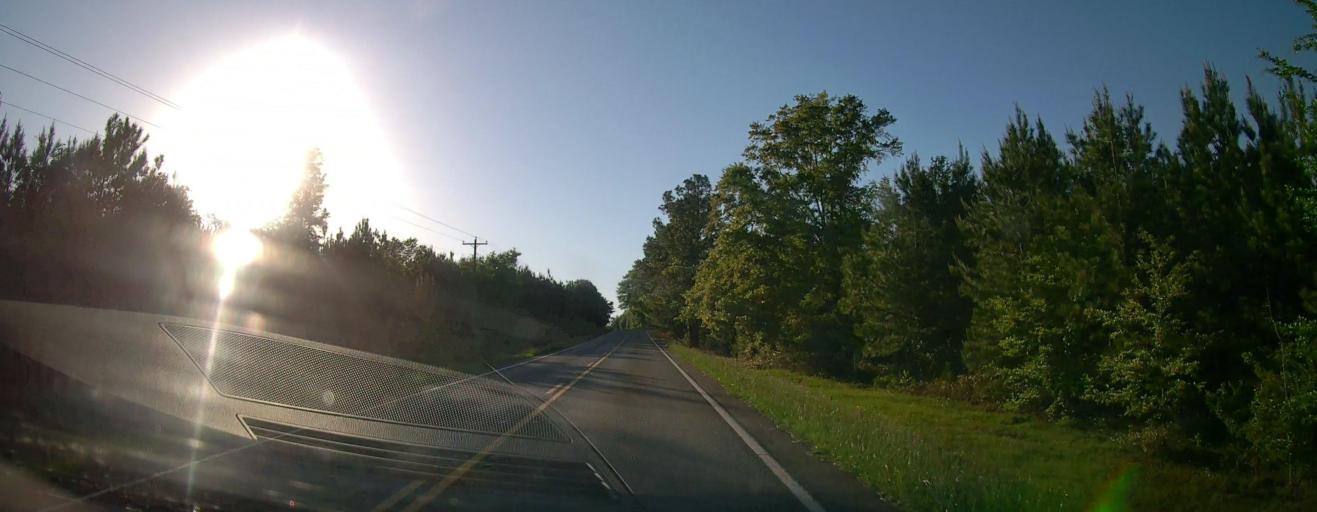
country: US
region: Georgia
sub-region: Macon County
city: Oglethorpe
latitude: 32.3147
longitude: -84.1672
